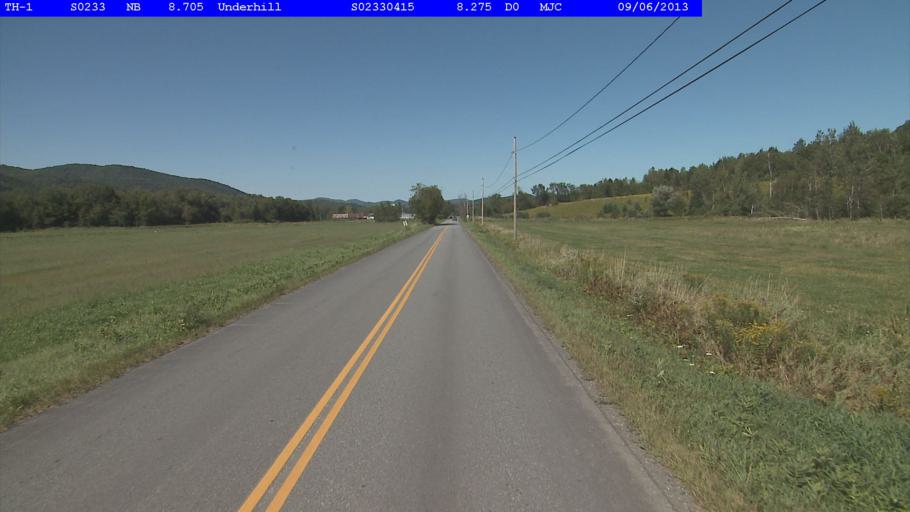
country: US
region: Vermont
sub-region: Chittenden County
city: Jericho
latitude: 44.5838
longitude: -72.8634
